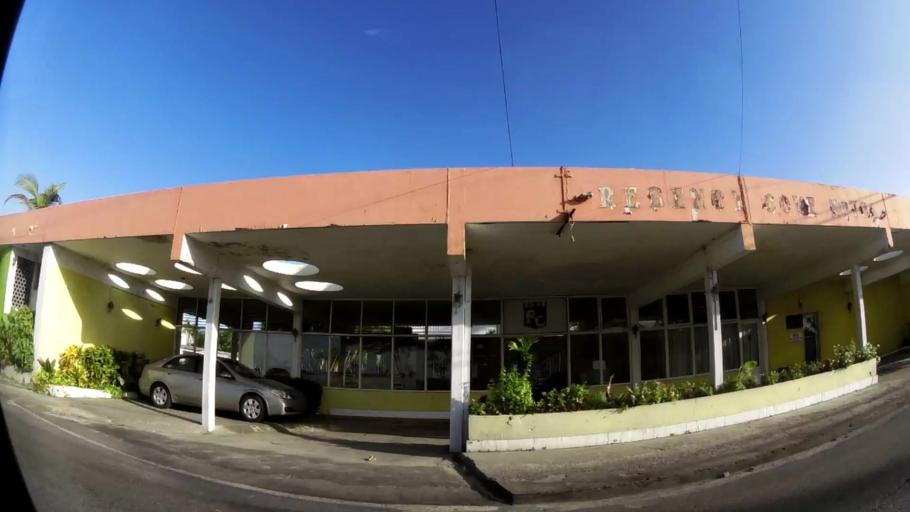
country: BB
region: Saint Michael
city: Bridgetown
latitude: 13.0741
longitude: -59.5953
